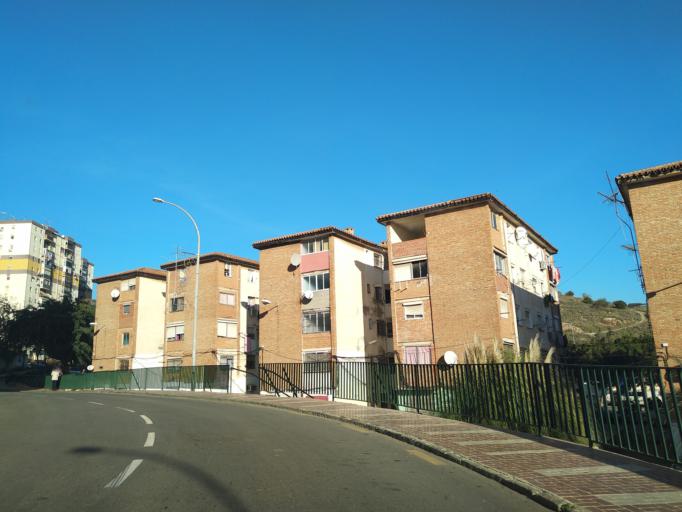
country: ES
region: Andalusia
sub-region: Provincia de Malaga
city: Malaga
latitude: 36.7412
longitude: -4.4304
